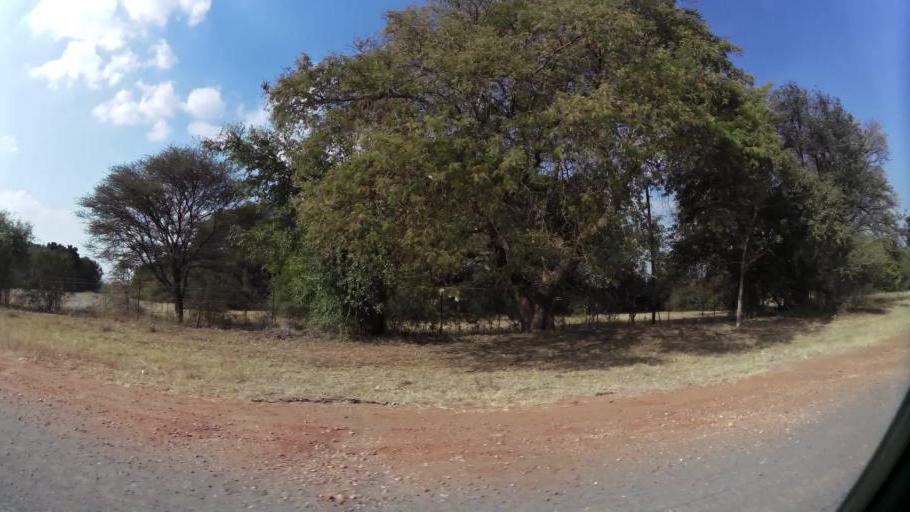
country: ZA
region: North-West
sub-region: Bojanala Platinum District Municipality
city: Mogwase
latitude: -25.4790
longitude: 27.0866
